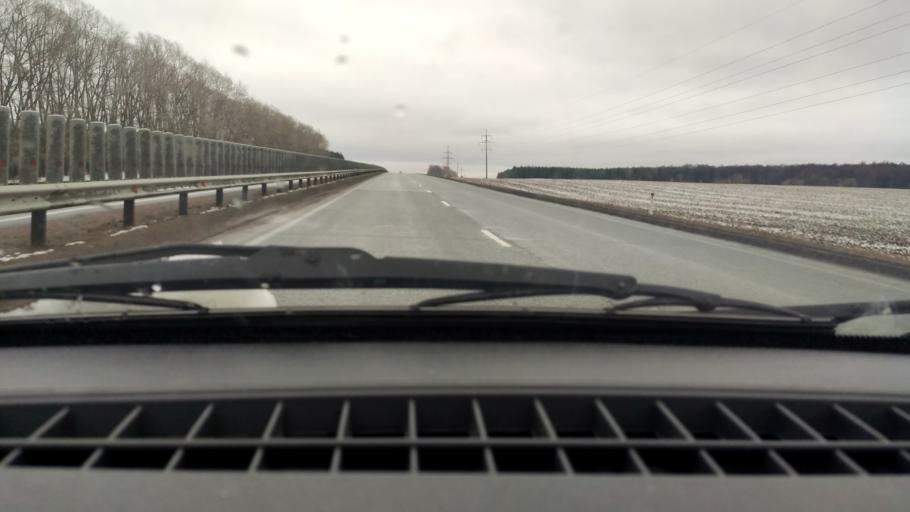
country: RU
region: Bashkortostan
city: Kushnarenkovo
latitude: 55.0527
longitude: 55.4375
